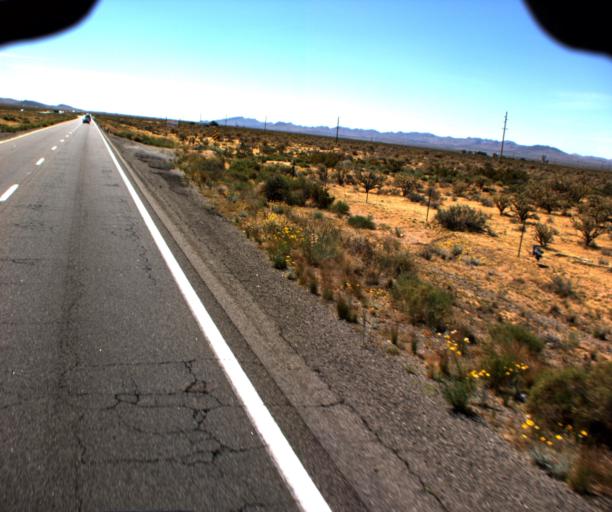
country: US
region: Arizona
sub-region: Mohave County
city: Dolan Springs
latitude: 35.5221
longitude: -114.3474
